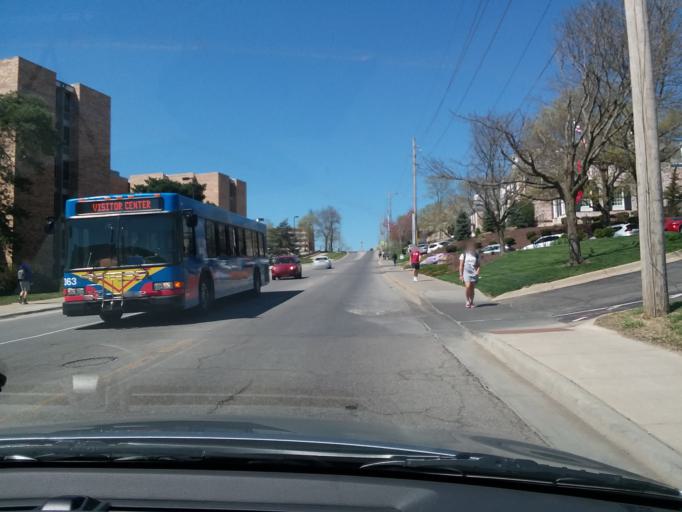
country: US
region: Kansas
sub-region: Douglas County
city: Lawrence
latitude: 38.9571
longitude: -95.2550
